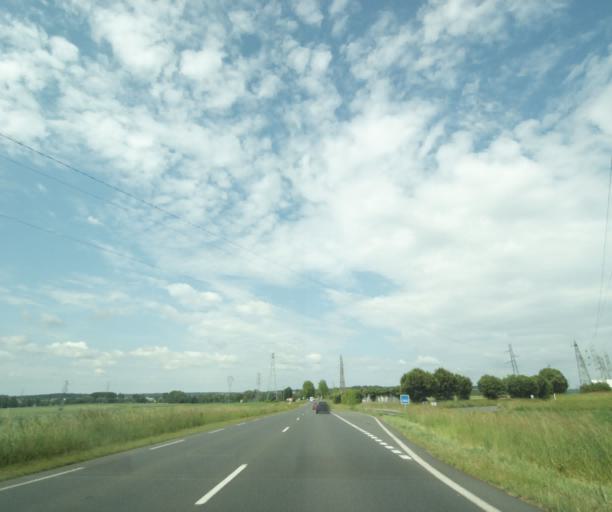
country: FR
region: Pays de la Loire
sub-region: Departement de Maine-et-Loire
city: Distre
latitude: 47.2086
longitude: -0.1187
